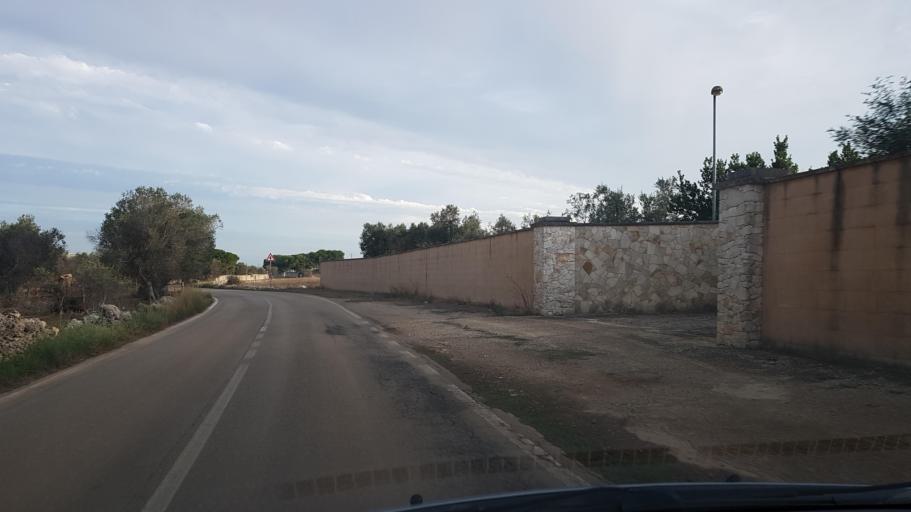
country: IT
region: Apulia
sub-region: Provincia di Lecce
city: Surbo
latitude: 40.4291
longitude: 18.1170
